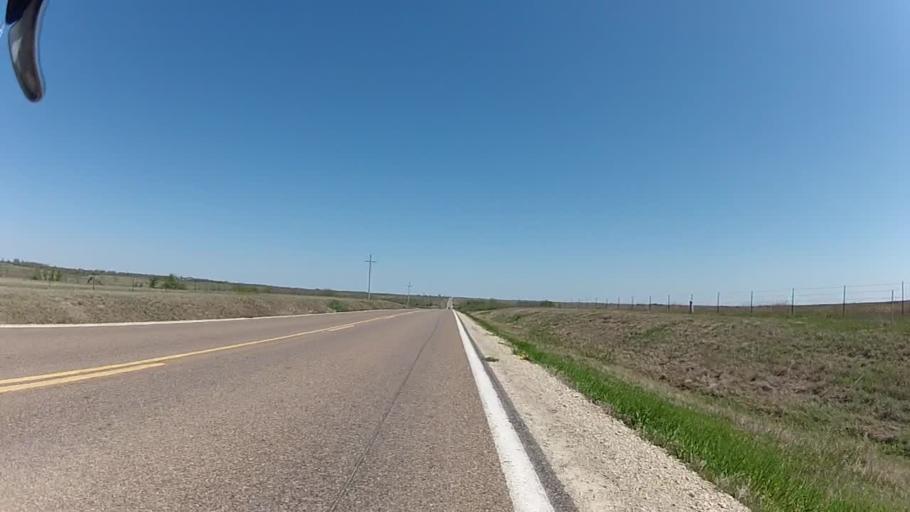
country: US
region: Kansas
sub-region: Morris County
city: Council Grove
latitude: 38.9014
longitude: -96.5202
